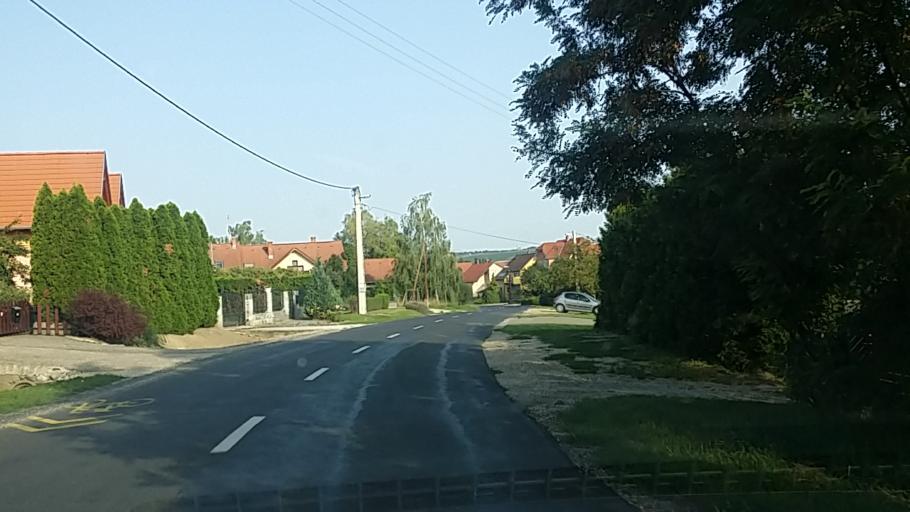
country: HU
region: Gyor-Moson-Sopron
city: Nagycenk
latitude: 47.6438
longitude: 16.6706
